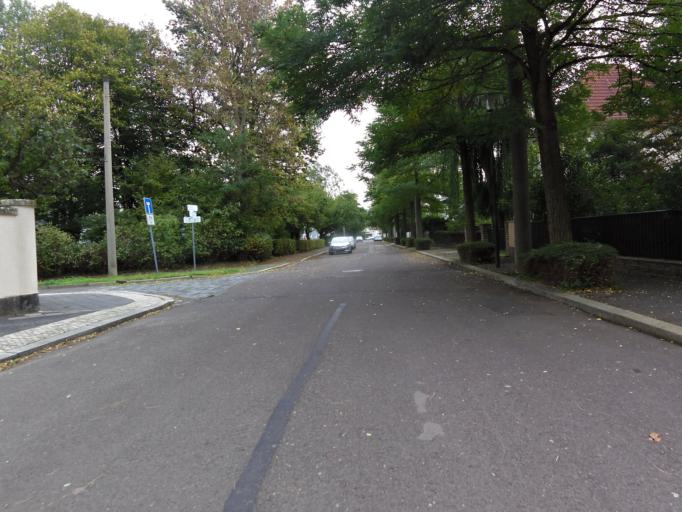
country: DE
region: Saxony
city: Markkleeberg
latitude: 51.2828
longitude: 12.3689
